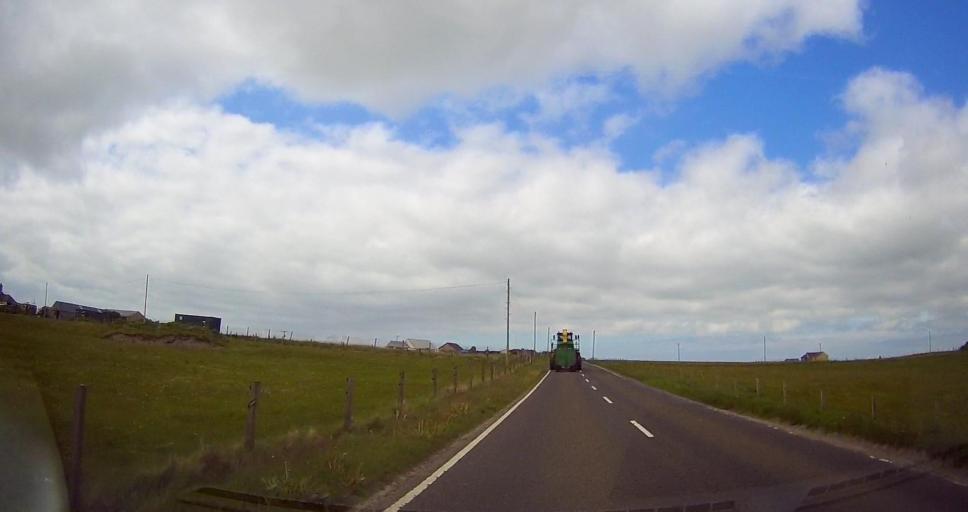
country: GB
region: Scotland
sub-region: Orkney Islands
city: Stromness
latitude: 59.0238
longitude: -3.1630
